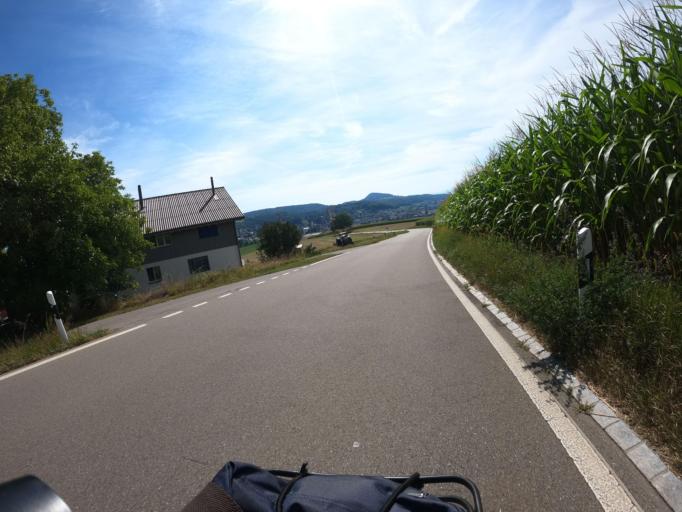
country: CH
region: Zurich
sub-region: Bezirk Affoltern
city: Hedingen
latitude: 47.3041
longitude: 8.4326
